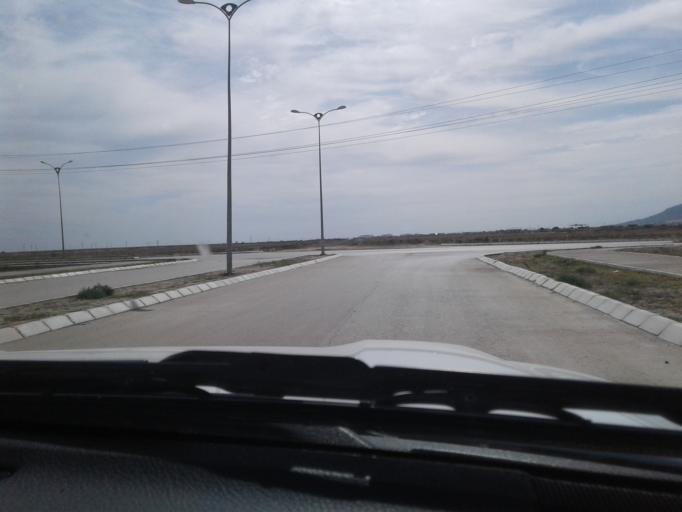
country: TM
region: Balkan
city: Gazanjyk
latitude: 39.2656
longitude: 55.4986
